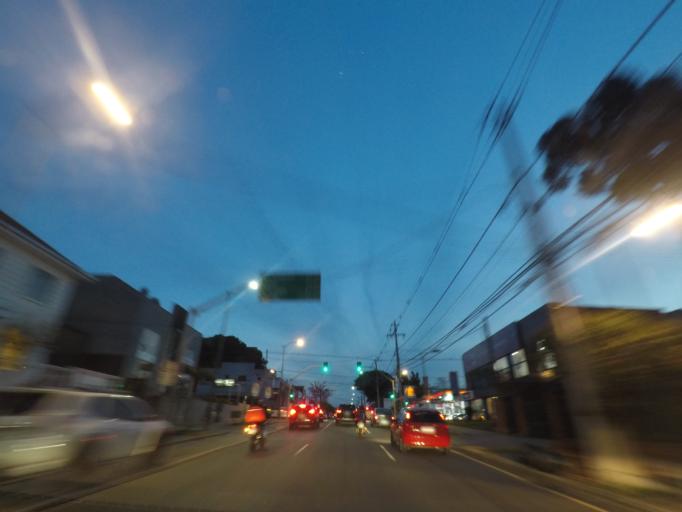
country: BR
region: Parana
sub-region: Curitiba
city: Curitiba
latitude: -25.4376
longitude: -49.2915
